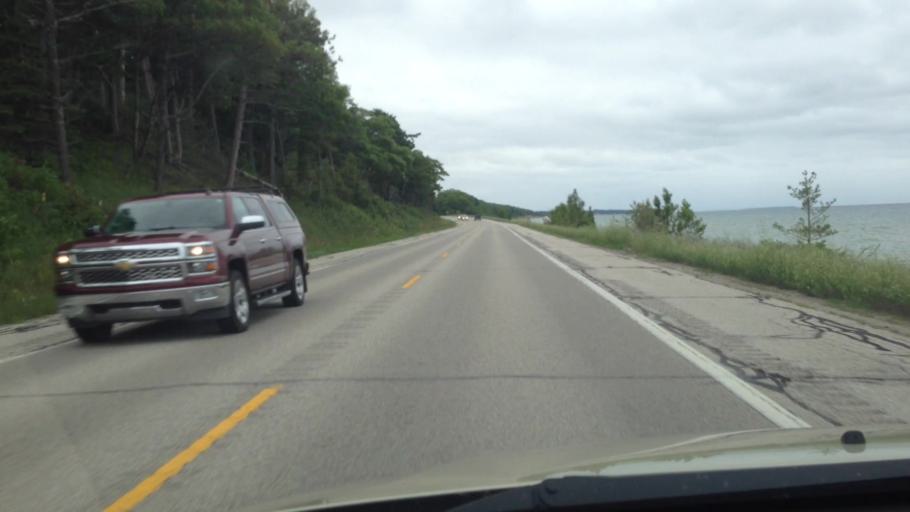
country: US
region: Michigan
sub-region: Mackinac County
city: Saint Ignace
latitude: 45.9927
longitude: -84.9834
